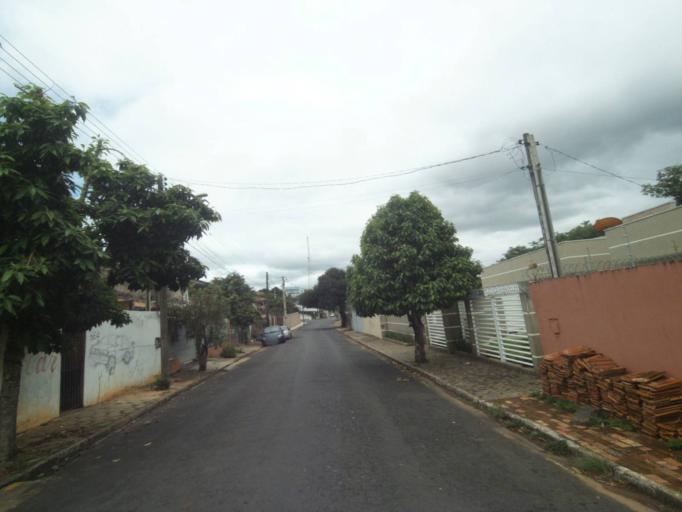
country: BR
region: Parana
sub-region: Telemaco Borba
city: Telemaco Borba
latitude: -24.3297
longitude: -50.6119
